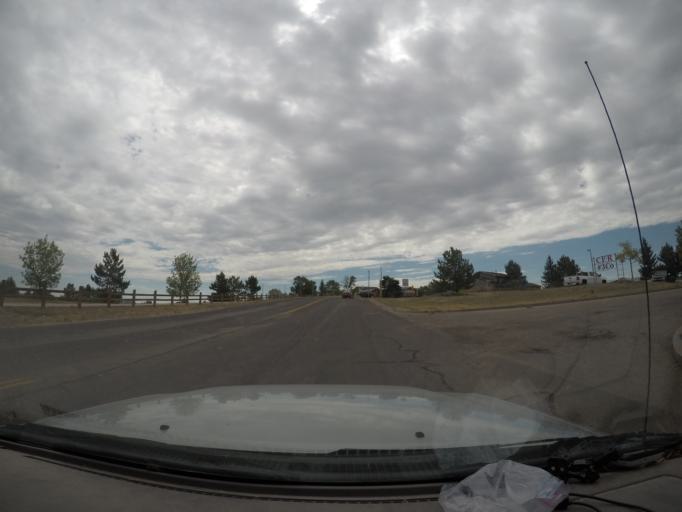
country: US
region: Wyoming
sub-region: Laramie County
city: Fox Farm-College
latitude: 41.1425
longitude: -104.7573
